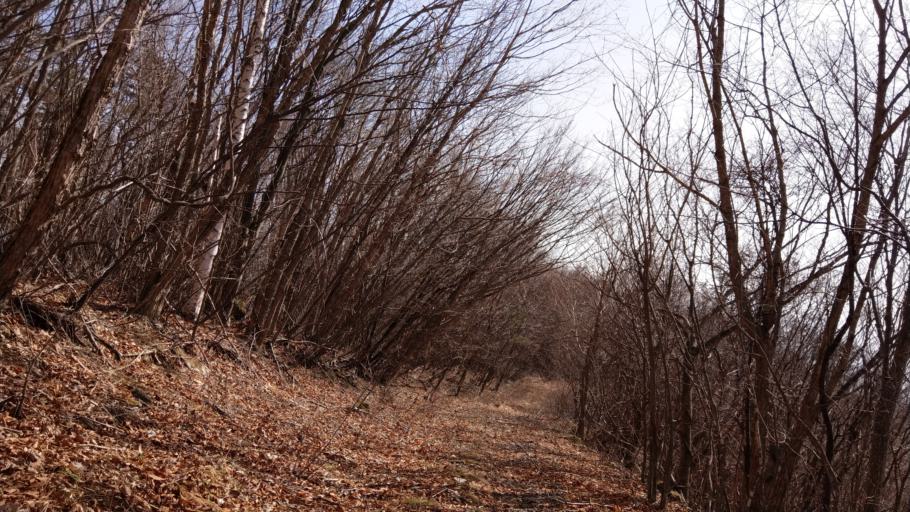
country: JP
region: Nagano
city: Komoro
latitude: 36.3814
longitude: 138.4396
